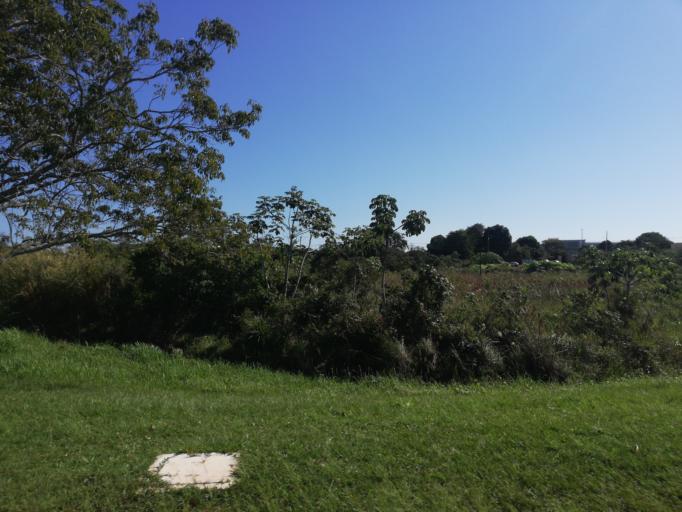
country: AR
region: Misiones
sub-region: Departamento de Iguazu
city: Puerto Iguazu
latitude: -25.5784
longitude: -54.5577
